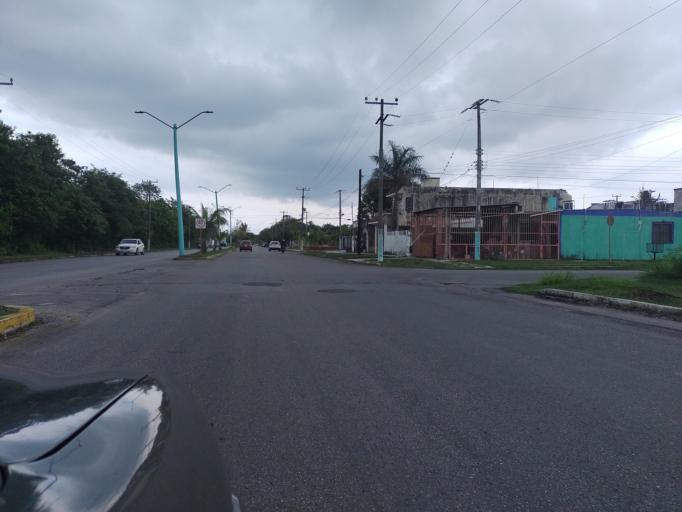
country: MX
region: Quintana Roo
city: Chetumal
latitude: 18.5074
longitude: -88.2835
